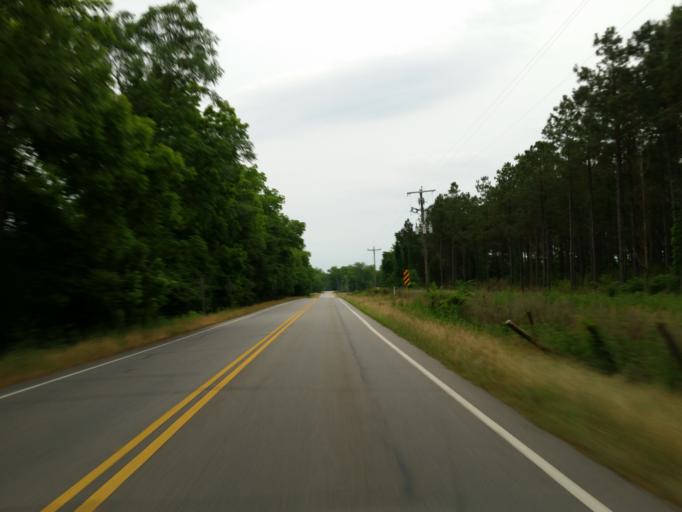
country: US
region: Georgia
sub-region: Dooly County
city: Vienna
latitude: 32.1435
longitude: -83.7989
